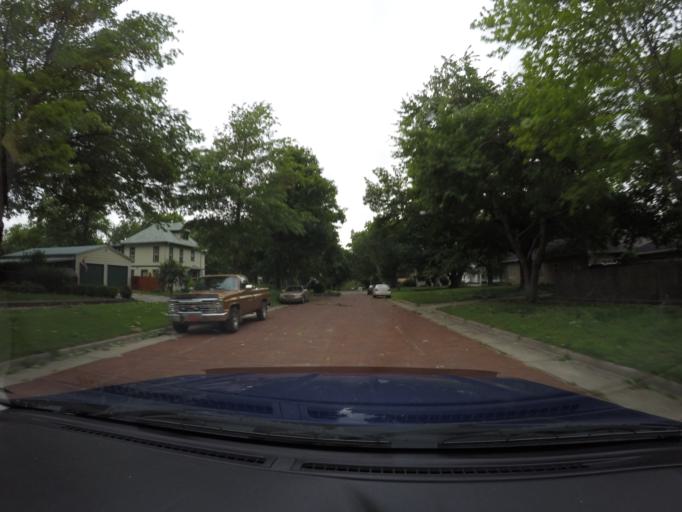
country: US
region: Kansas
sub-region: Clay County
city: Clay Center
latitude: 39.3866
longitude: -97.1257
